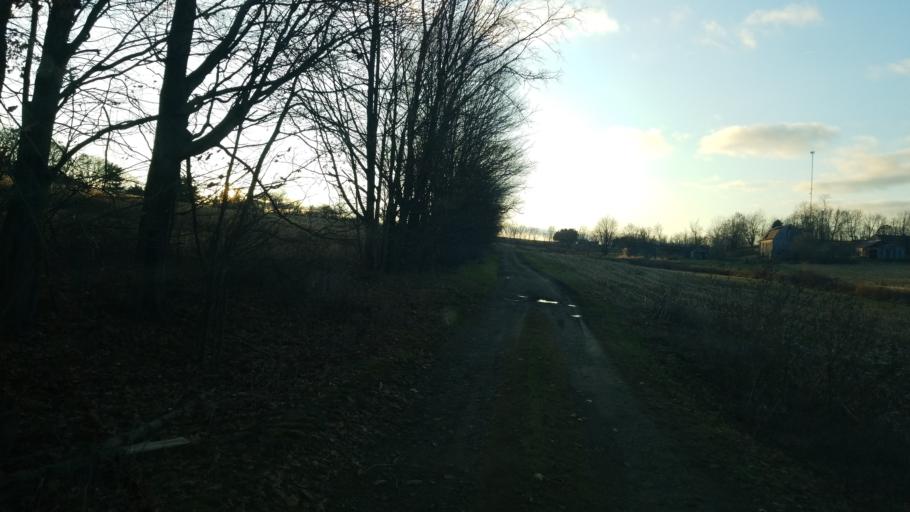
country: US
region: Ohio
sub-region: Sandusky County
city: Bellville
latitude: 40.5969
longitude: -82.5500
